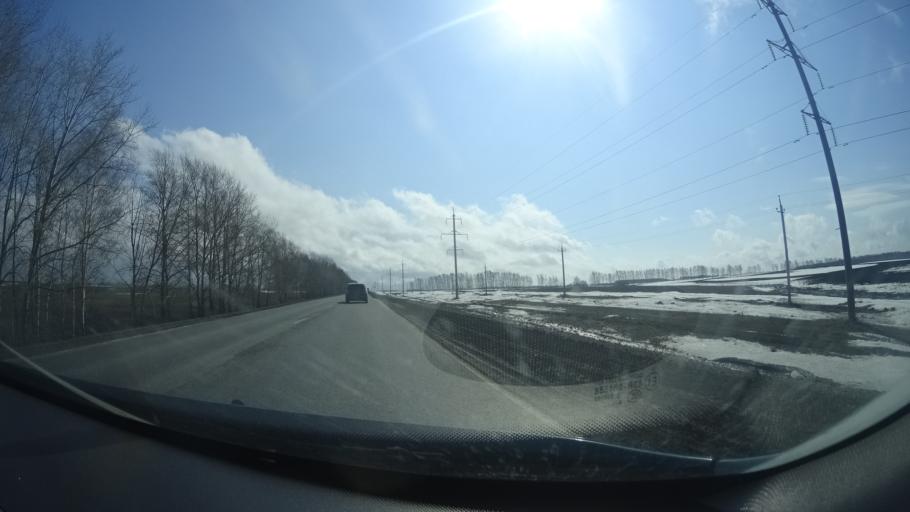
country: RU
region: Bashkortostan
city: Mikhaylovka
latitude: 54.8595
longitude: 55.7585
